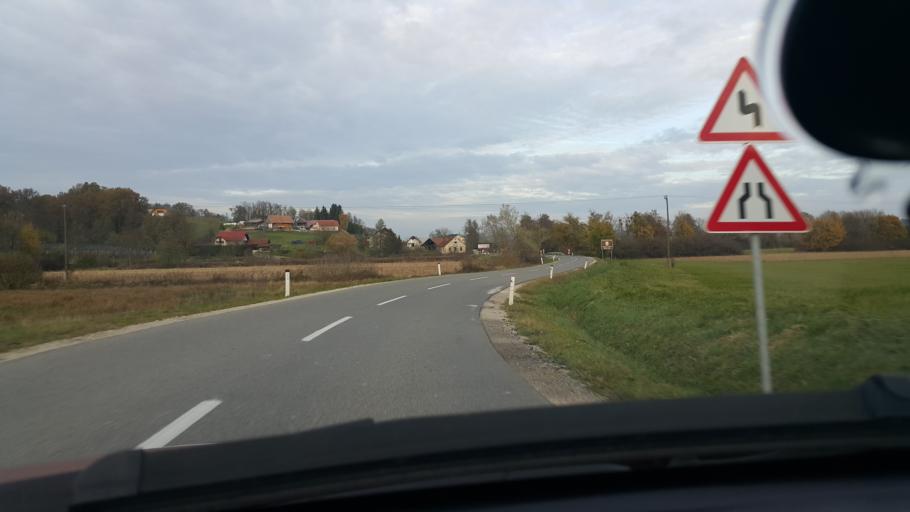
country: SI
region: Bistrica ob Sotli
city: Bistrica ob Sotli
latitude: 45.9633
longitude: 15.6908
